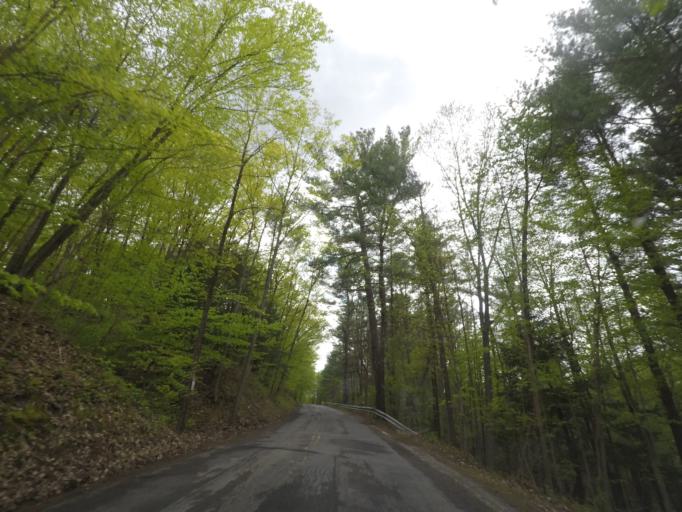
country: US
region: New York
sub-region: Albany County
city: Voorheesville
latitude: 42.6901
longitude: -73.9238
